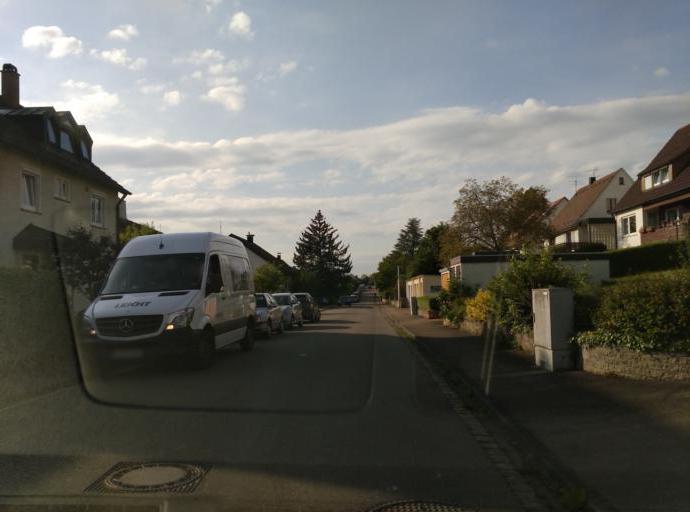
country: DE
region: Baden-Wuerttemberg
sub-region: Regierungsbezirk Stuttgart
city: Nurtingen
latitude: 48.6269
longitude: 9.3519
